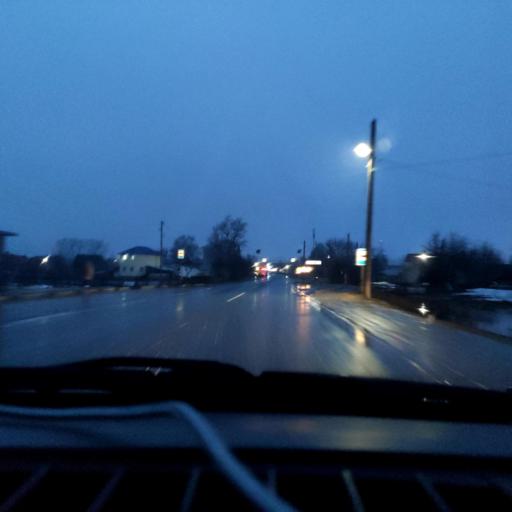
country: RU
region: Perm
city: Ust'-Kachka
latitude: 57.9896
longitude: 55.7146
